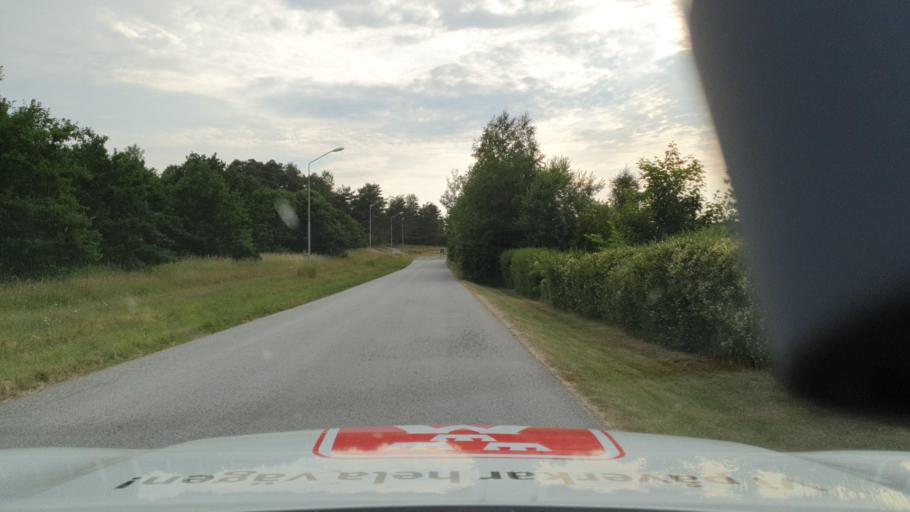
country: SE
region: Skane
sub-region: Sjobo Kommun
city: Sjoebo
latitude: 55.6287
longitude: 13.7212
